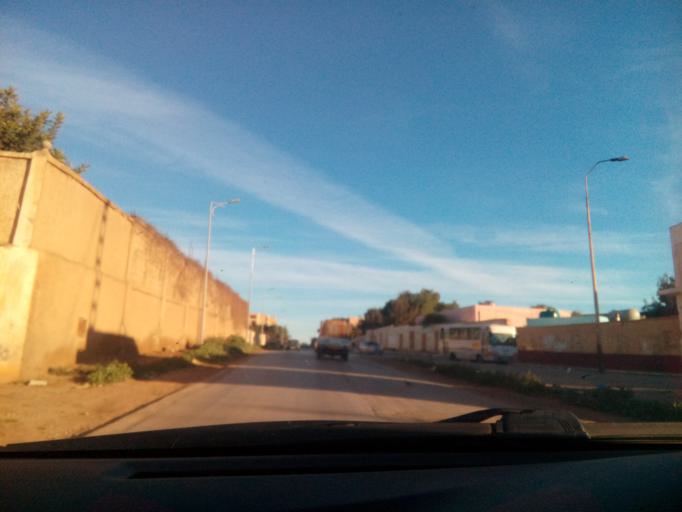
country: DZ
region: Oran
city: Es Senia
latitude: 35.6392
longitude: -0.6727
